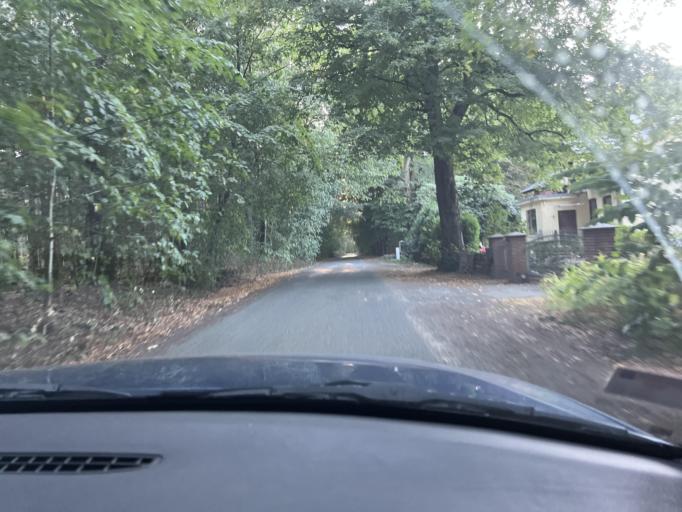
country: DE
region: Schleswig-Holstein
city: Weddingstedt
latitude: 54.2247
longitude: 9.1077
